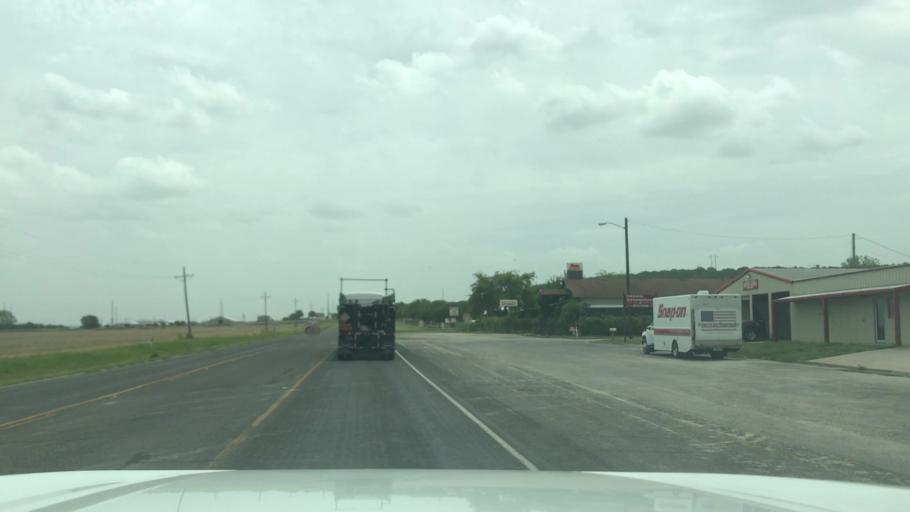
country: US
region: Texas
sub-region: Bosque County
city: Clifton
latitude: 31.7755
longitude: -97.5733
